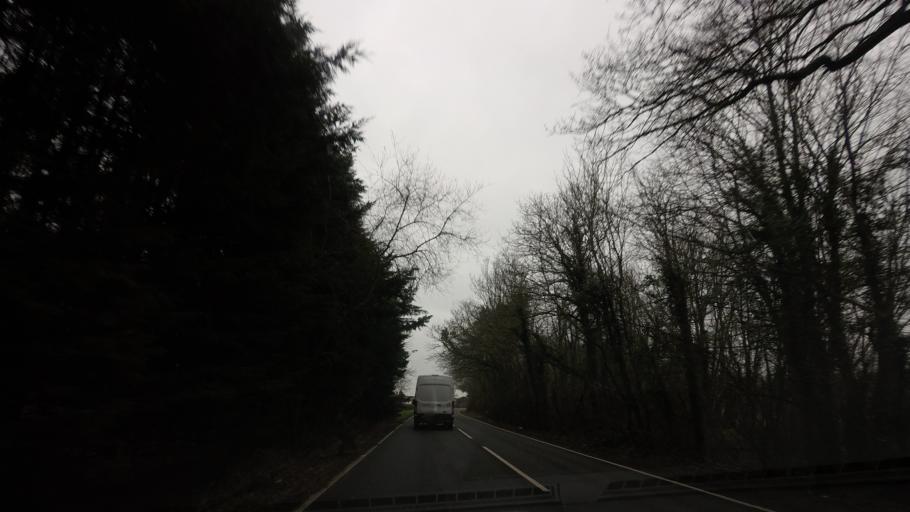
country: GB
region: England
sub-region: Kent
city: Staplehurst
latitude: 51.1445
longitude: 0.5513
